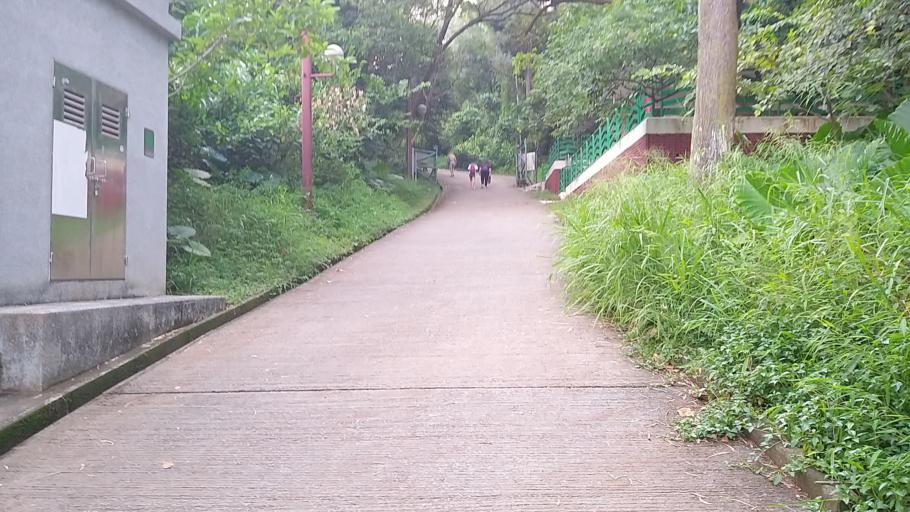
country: HK
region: Tuen Mun
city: Tuen Mun
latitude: 22.4046
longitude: 113.9581
